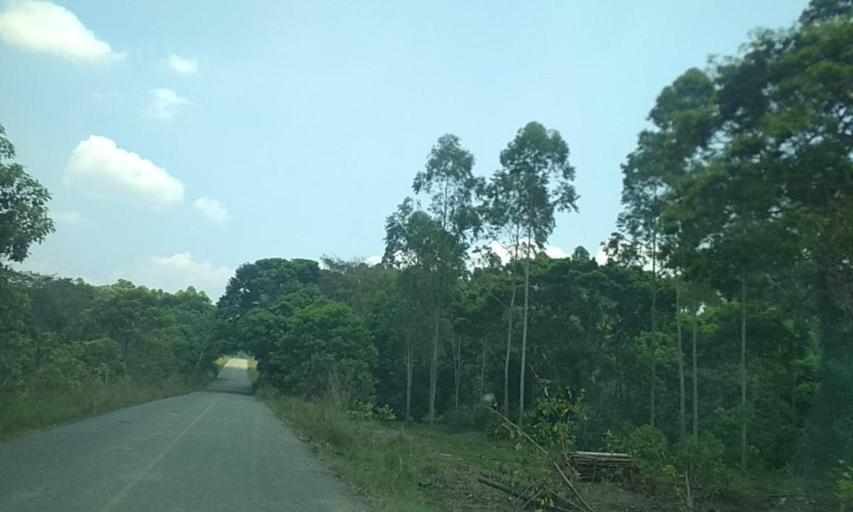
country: MX
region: Tabasco
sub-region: Huimanguillo
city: Francisco Rueda
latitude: 17.8416
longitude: -93.8909
